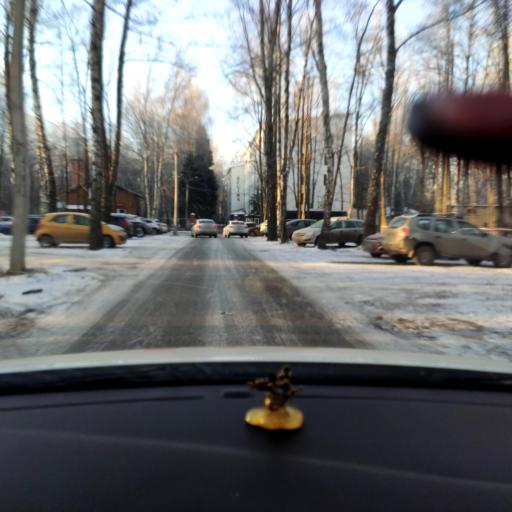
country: RU
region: Tatarstan
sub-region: Gorod Kazan'
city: Kazan
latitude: 55.6769
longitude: 49.0992
